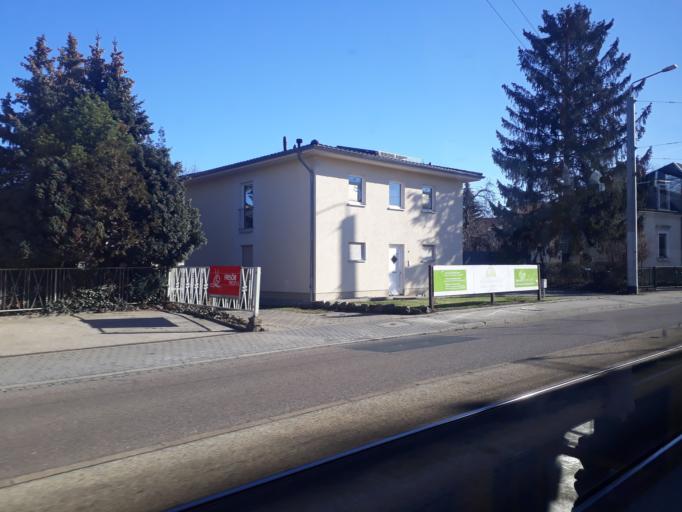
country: DE
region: Saxony
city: Heidenau
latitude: 51.0223
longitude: 13.8111
